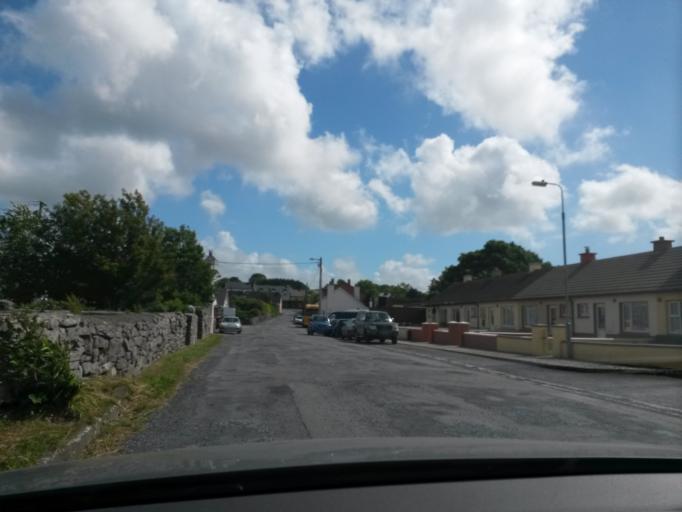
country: IE
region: Connaught
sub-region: County Galway
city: Bearna
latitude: 52.9921
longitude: -9.2152
